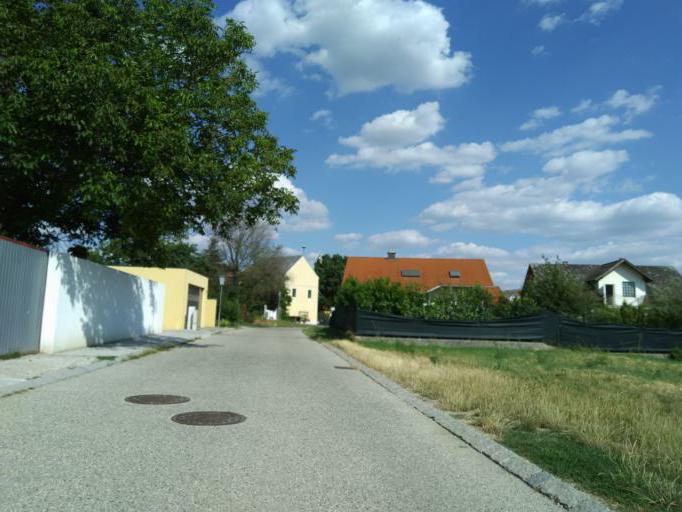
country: AT
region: Lower Austria
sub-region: Politischer Bezirk Mistelbach
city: Gross-Engersdorf
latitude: 48.3575
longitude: 16.5656
